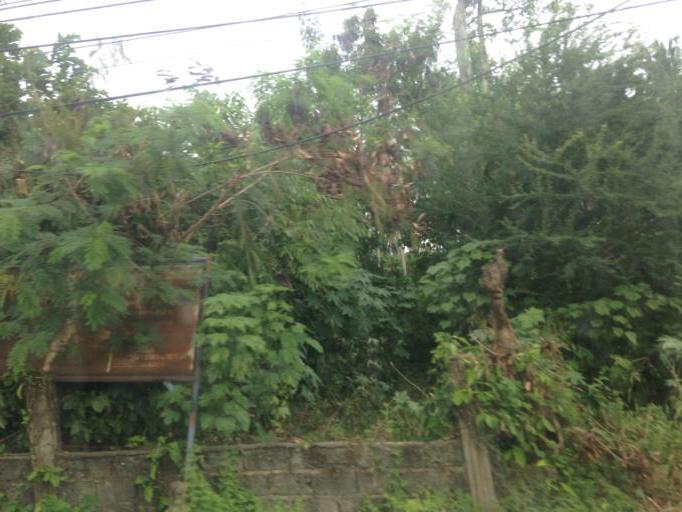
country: PH
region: Mimaropa
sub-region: Province of Mindoro Oriental
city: San Aquilino
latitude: 12.5989
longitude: 121.4847
